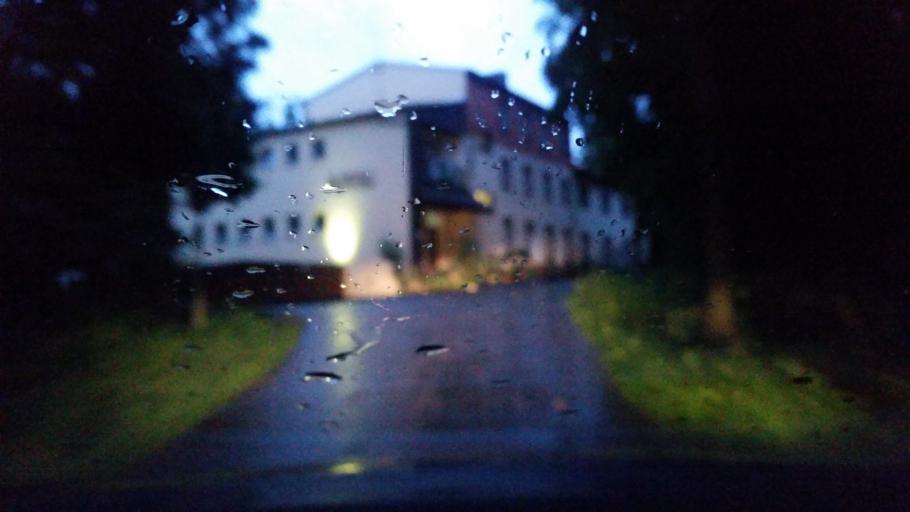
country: DE
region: Saxony
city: Sohland am Rotstein
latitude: 51.1083
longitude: 14.7645
